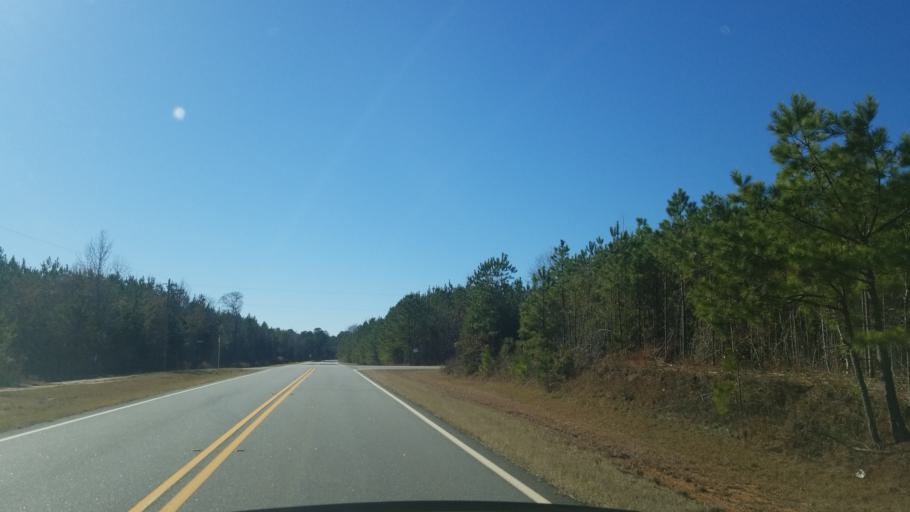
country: US
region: Georgia
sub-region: Talbot County
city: Sardis
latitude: 32.6360
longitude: -84.7208
